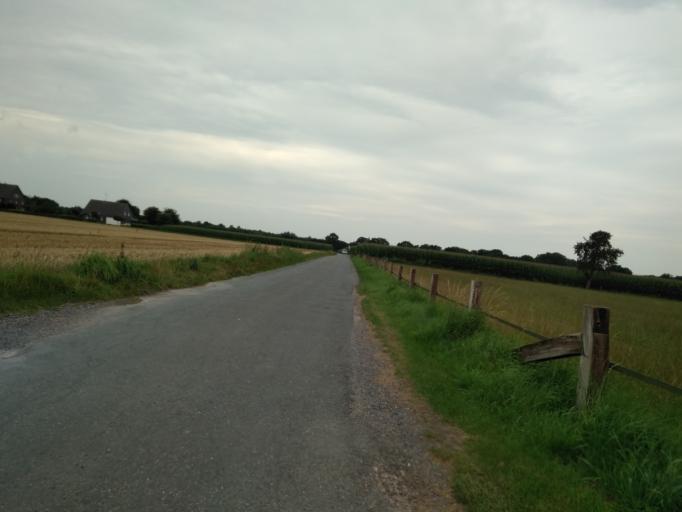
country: DE
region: North Rhine-Westphalia
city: Dorsten
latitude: 51.6065
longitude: 6.9031
